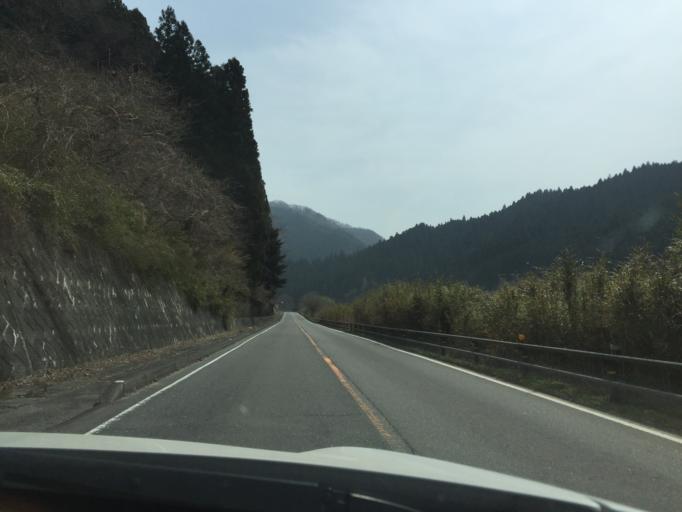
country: JP
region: Fukushima
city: Ishikawa
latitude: 37.0622
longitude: 140.5840
